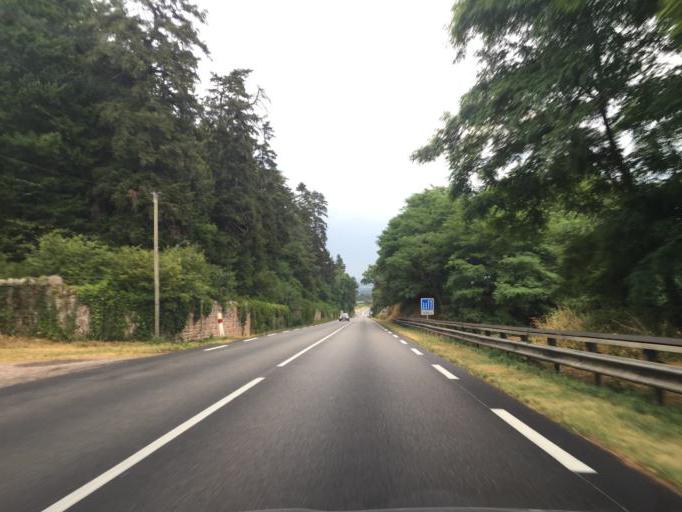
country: FR
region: Rhone-Alpes
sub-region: Departement de la Loire
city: La Pacaudiere
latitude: 46.1947
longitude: 3.8450
